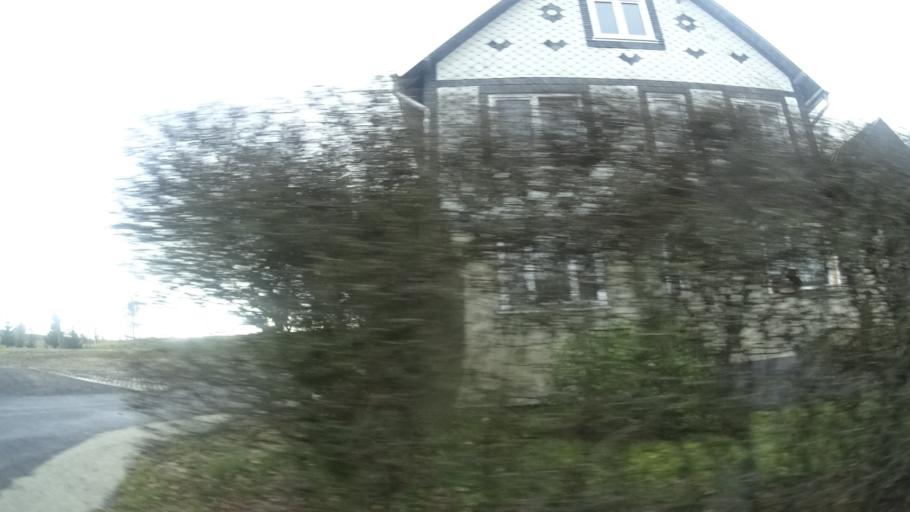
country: DE
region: Thuringia
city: Wittgendorf
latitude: 50.6029
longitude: 11.2448
